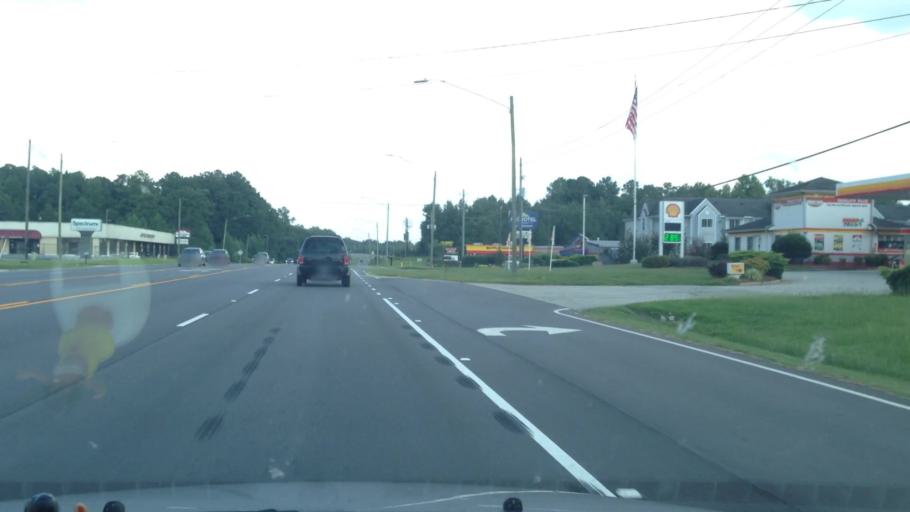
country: US
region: North Carolina
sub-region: Harnett County
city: Lillington
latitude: 35.4163
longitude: -78.8003
